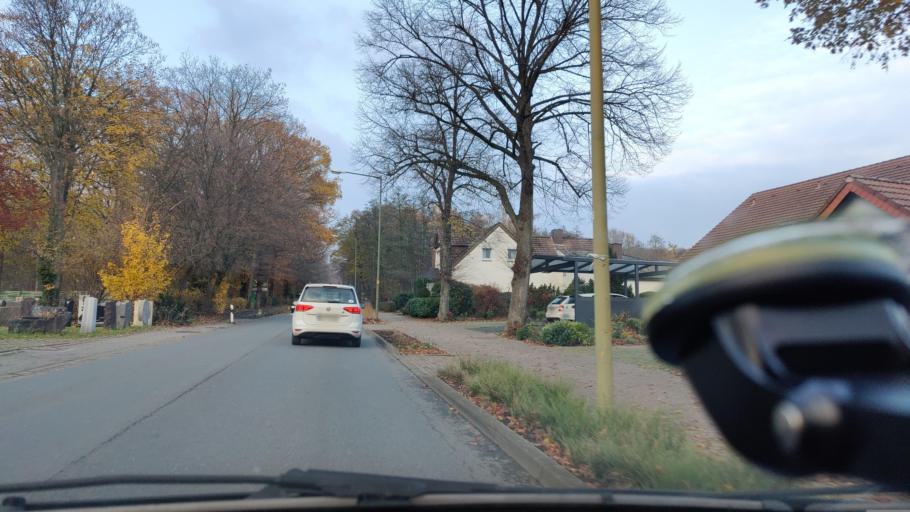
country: DE
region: North Rhine-Westphalia
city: Lunen
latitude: 51.6354
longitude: 7.5279
